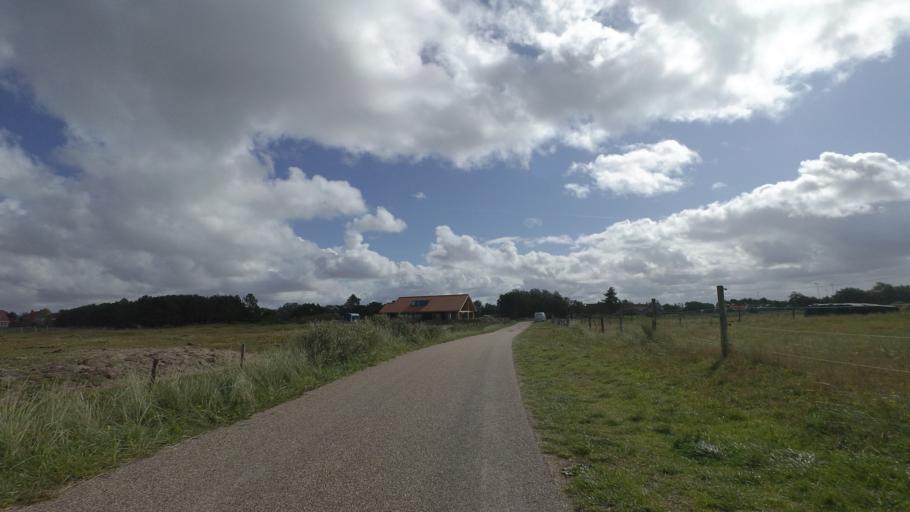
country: NL
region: Friesland
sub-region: Gemeente Ameland
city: Nes
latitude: 53.4505
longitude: 5.7931
